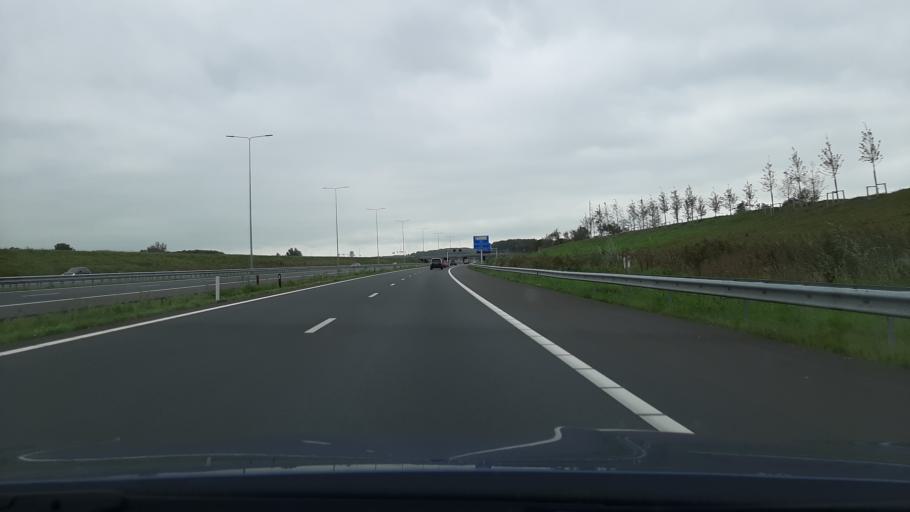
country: NL
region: Flevoland
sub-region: Gemeente Almere
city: Almere Stad
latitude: 52.3535
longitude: 5.2235
